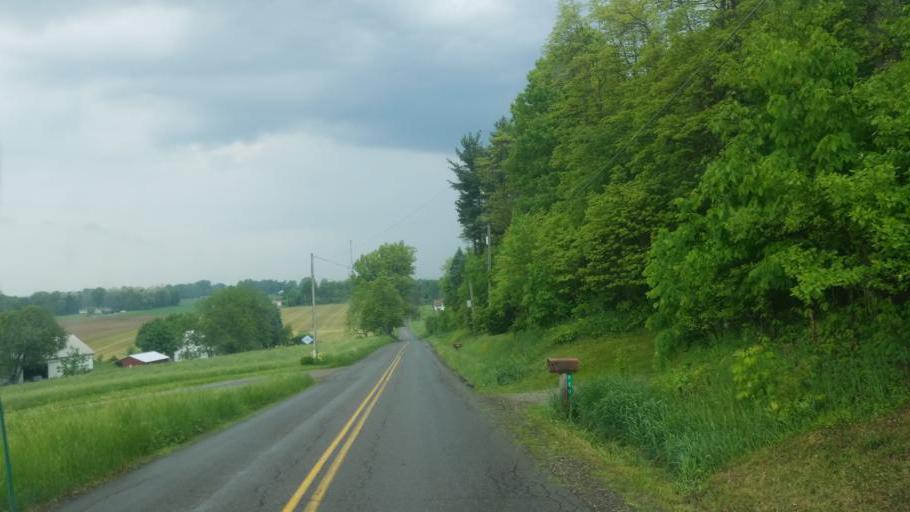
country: US
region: Ohio
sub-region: Wayne County
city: Dalton
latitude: 40.7867
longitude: -81.7070
